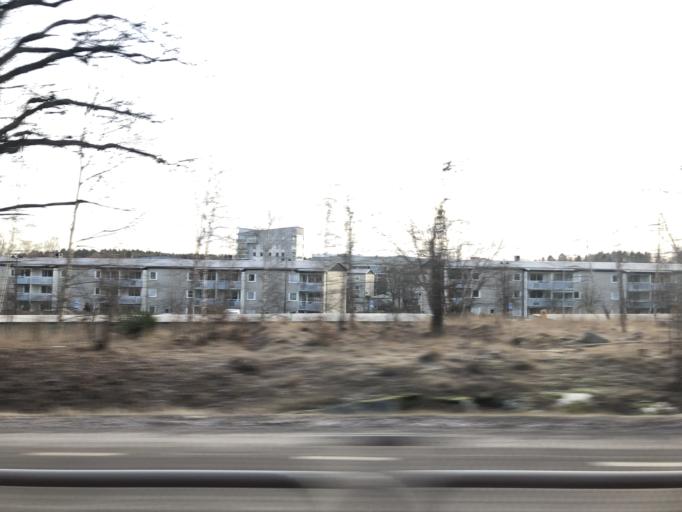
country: SE
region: Stockholm
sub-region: Jarfalla Kommun
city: Jakobsberg
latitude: 59.4123
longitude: 17.7967
